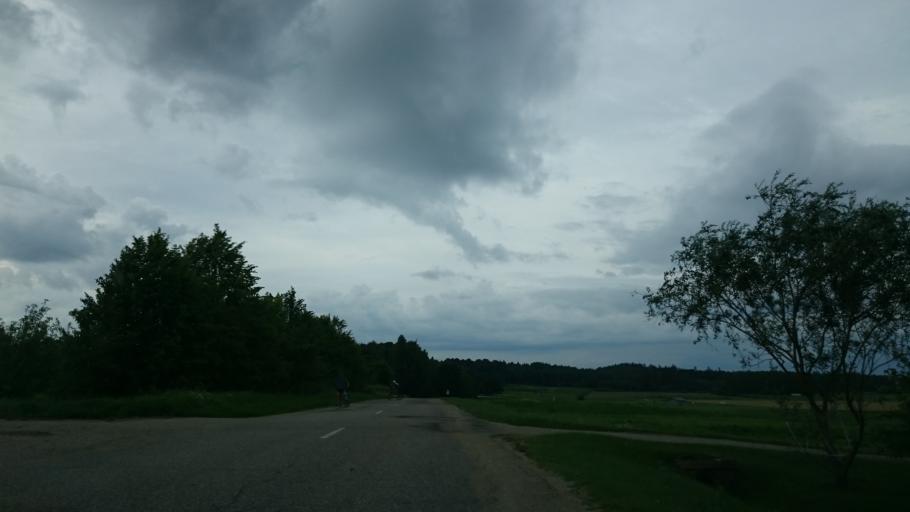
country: LV
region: Seja
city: Loja
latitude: 57.2064
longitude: 24.5881
